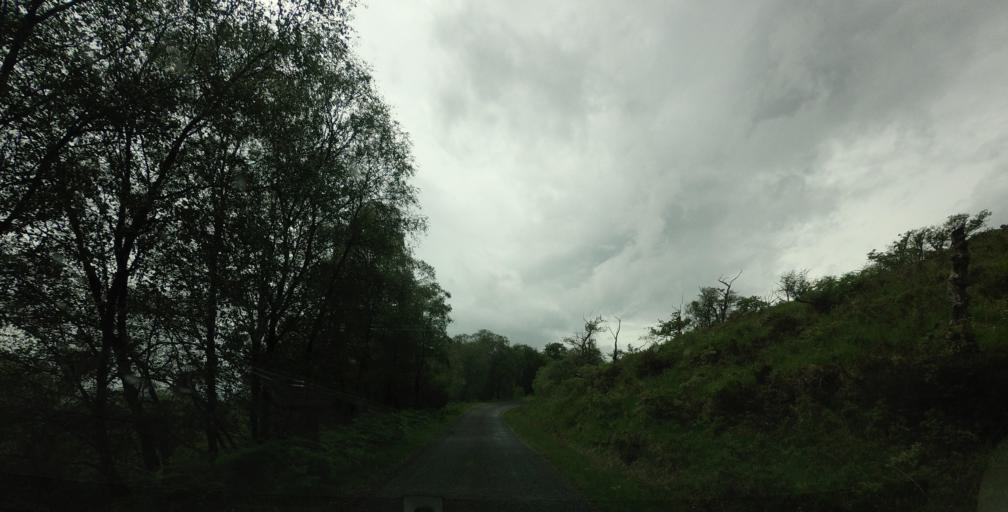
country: GB
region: Scotland
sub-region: Highland
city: Fort William
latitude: 56.7759
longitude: -5.2041
